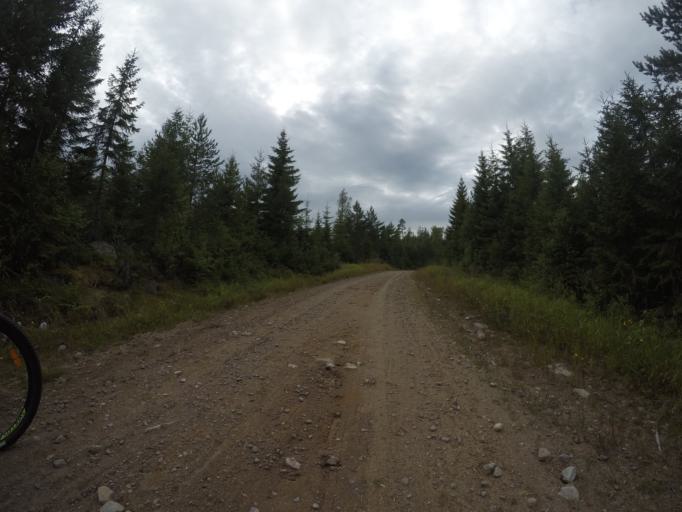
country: SE
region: OErebro
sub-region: Hallefors Kommun
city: Haellefors
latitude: 60.0164
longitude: 14.4701
